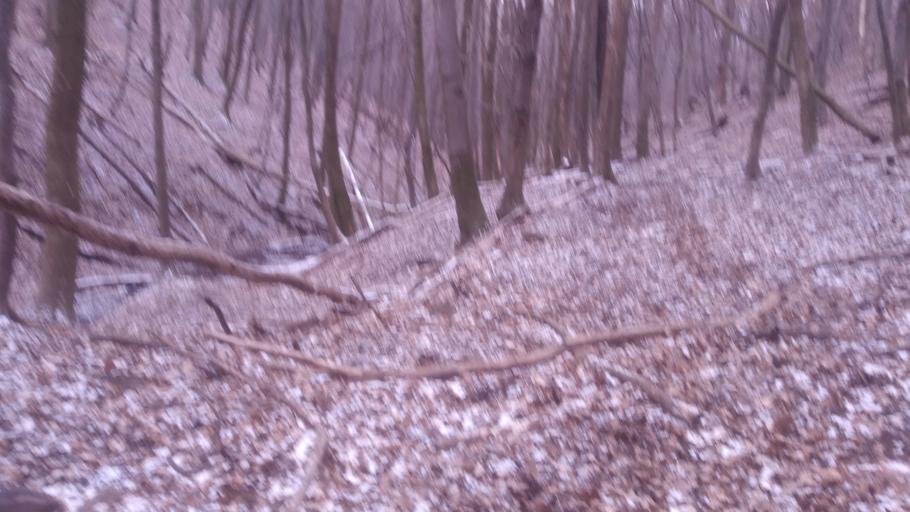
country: SK
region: Nitriansky
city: Sahy
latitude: 47.9586
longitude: 18.9124
